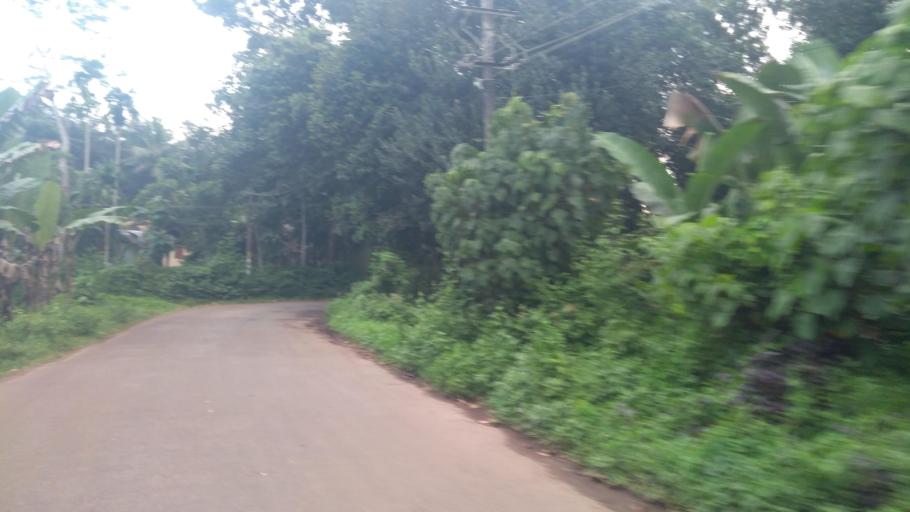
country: IN
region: Kerala
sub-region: Alappuzha
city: Kattanam
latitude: 9.1322
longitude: 76.6352
